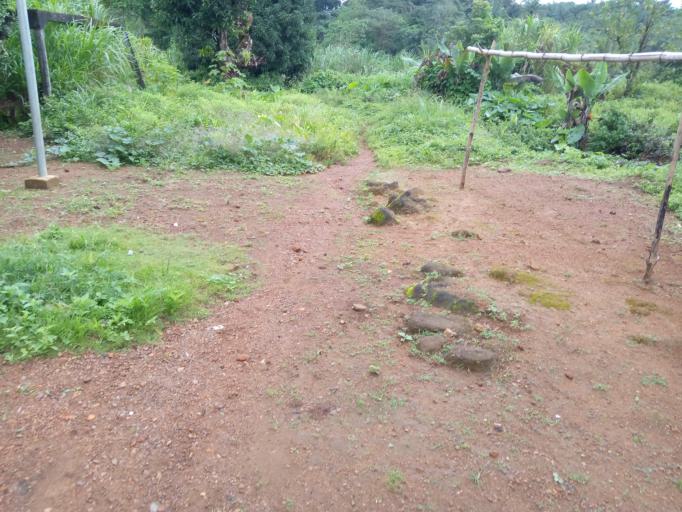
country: SL
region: Eastern Province
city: Buedu
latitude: 8.4645
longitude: -10.3362
